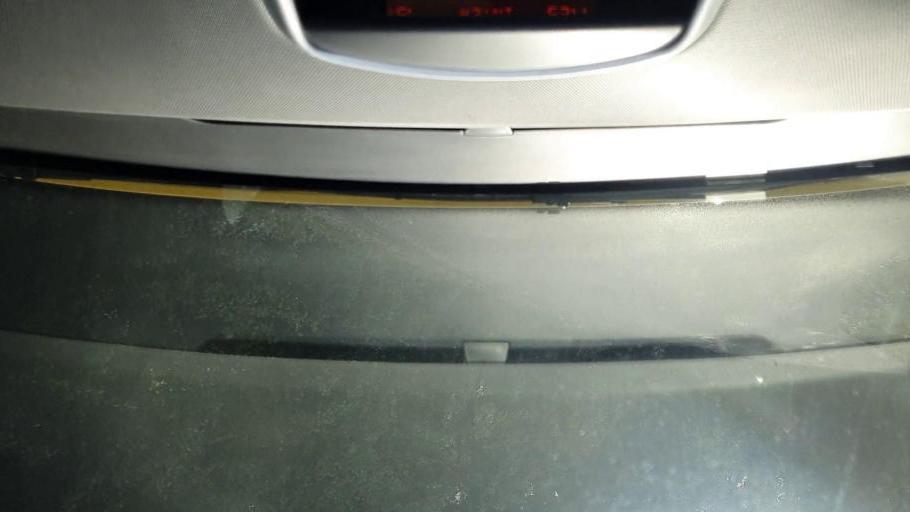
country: FR
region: Languedoc-Roussillon
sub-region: Departement du Gard
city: Anduze
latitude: 44.0448
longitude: 3.9210
